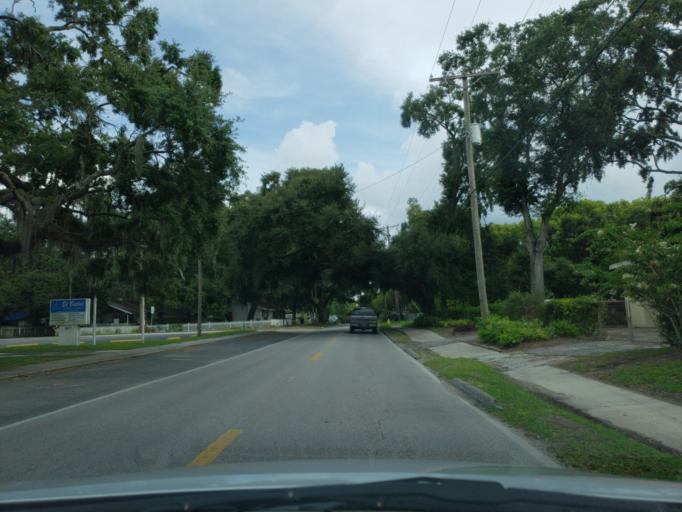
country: US
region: Florida
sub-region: Hillsborough County
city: Temple Terrace
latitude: 28.0079
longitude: -82.4430
